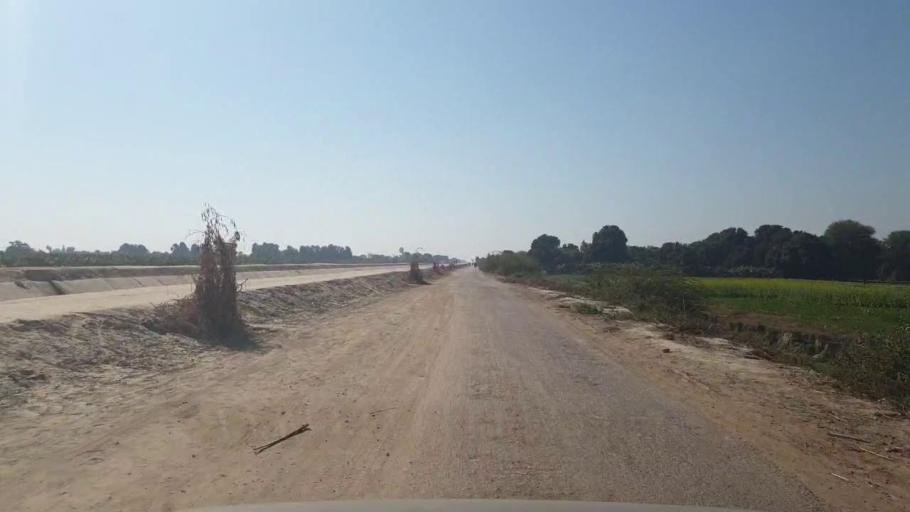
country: PK
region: Sindh
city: Mirwah Gorchani
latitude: 25.3032
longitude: 69.1029
